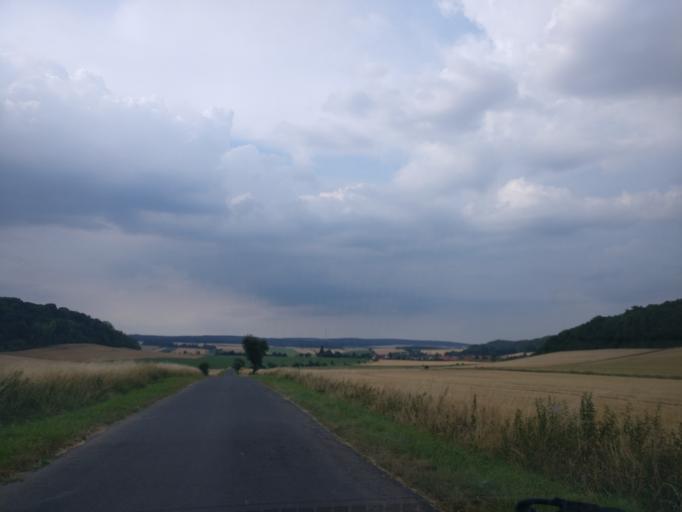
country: DE
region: Lower Saxony
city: Adelebsen
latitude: 51.5833
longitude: 9.7804
